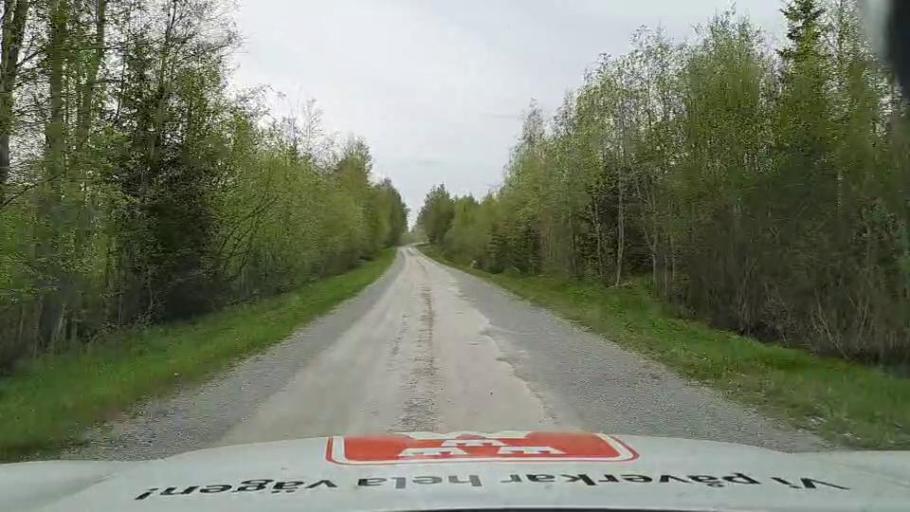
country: SE
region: Jaemtland
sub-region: Bergs Kommun
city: Hoverberg
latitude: 62.7498
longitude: 14.6632
